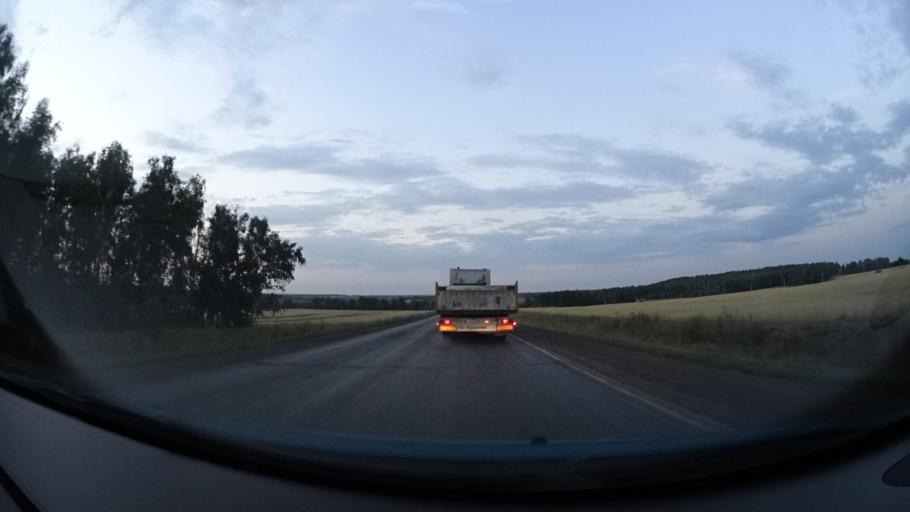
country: RU
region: Tatarstan
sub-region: Bavlinskiy Rayon
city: Bavly
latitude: 54.3022
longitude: 53.0140
